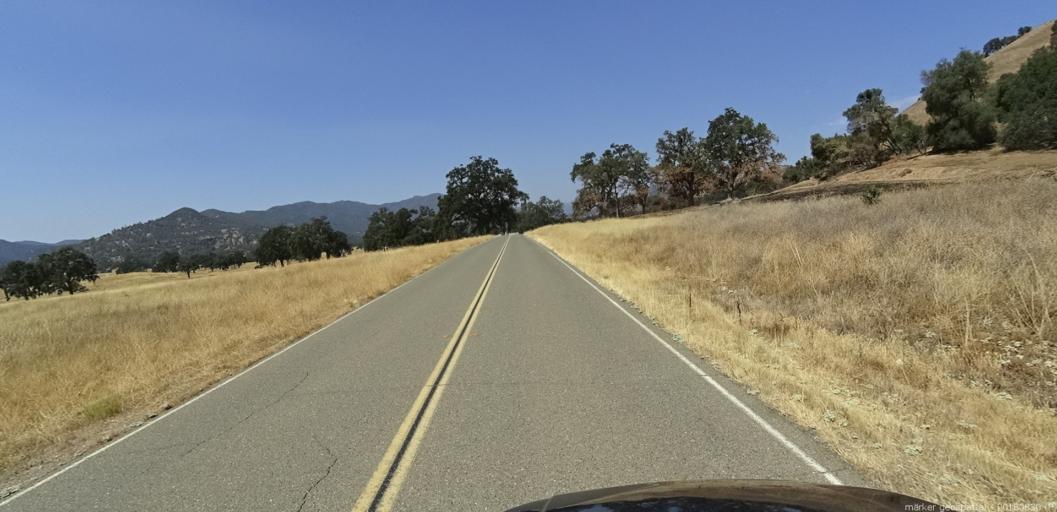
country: US
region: California
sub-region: Monterey County
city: King City
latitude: 35.9638
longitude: -121.2967
